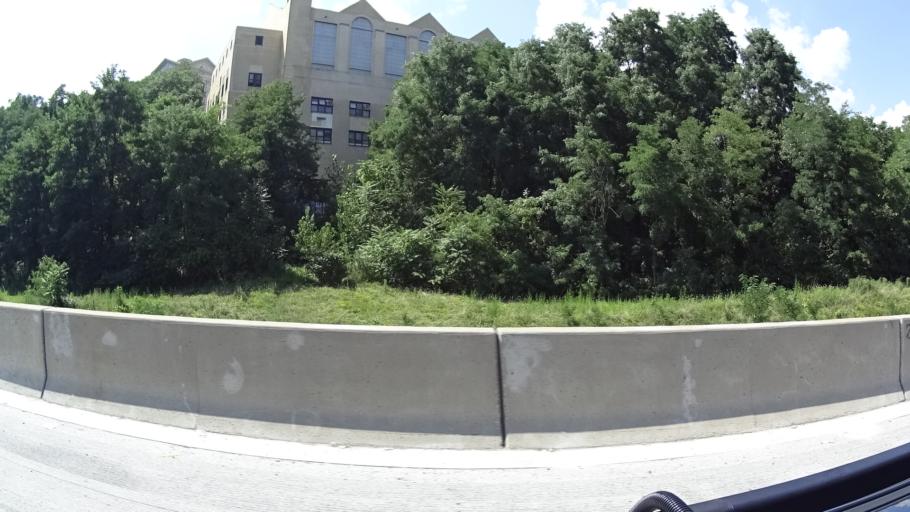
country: US
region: New Jersey
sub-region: Hudson County
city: Hoboken
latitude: 40.7306
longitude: -74.0518
